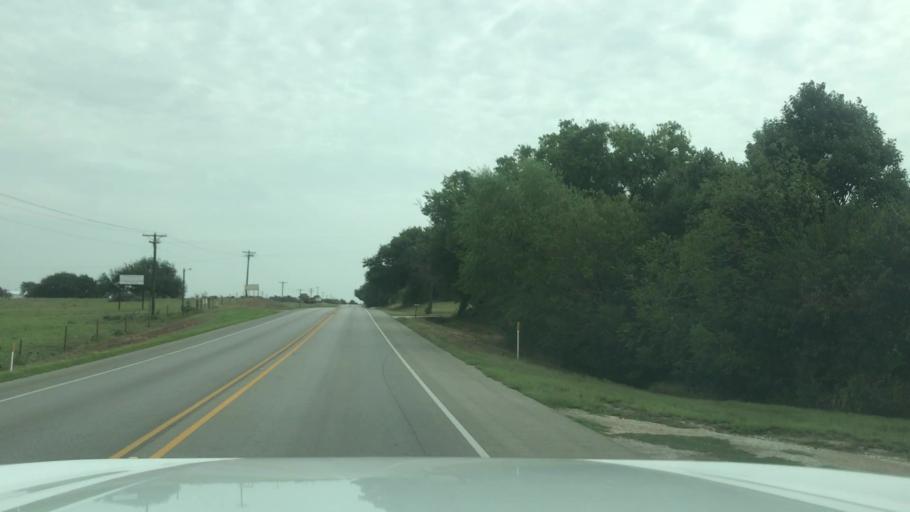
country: US
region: Texas
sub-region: Erath County
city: Dublin
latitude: 32.0920
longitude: -98.4181
